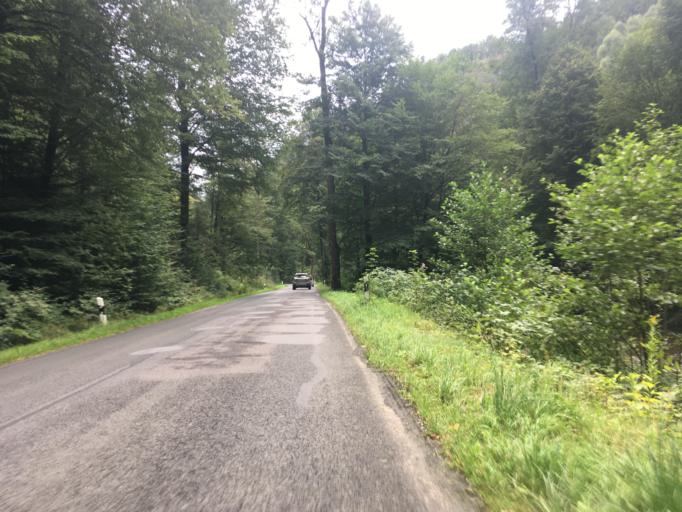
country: DE
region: Saxony
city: Sebnitz
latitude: 50.9347
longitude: 14.2669
